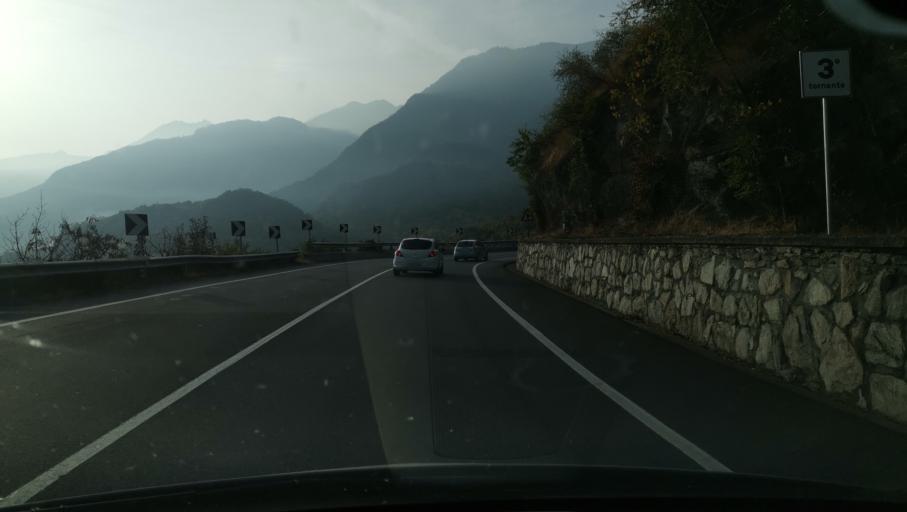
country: IT
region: Piedmont
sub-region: Provincia di Torino
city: San Giuseppe
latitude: 45.1319
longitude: 7.0403
